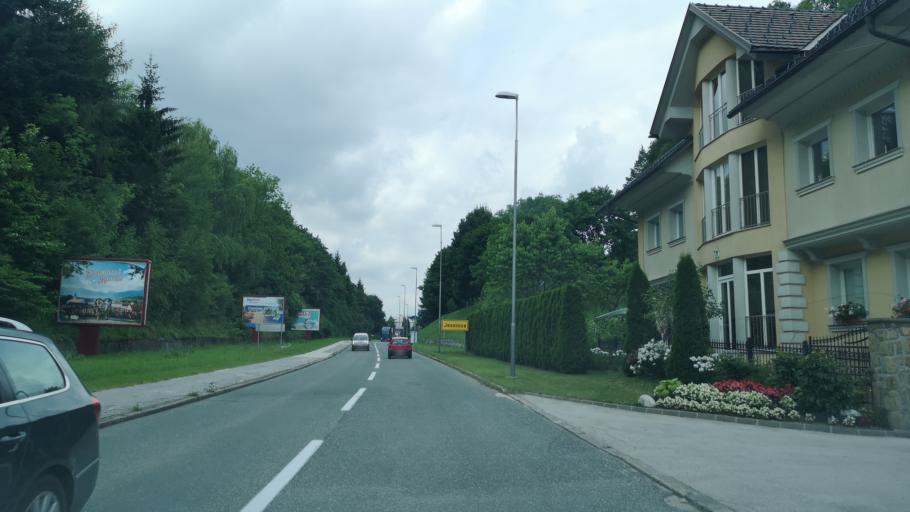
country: SI
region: Jesenice
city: Jesenice
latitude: 46.4292
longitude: 14.0772
